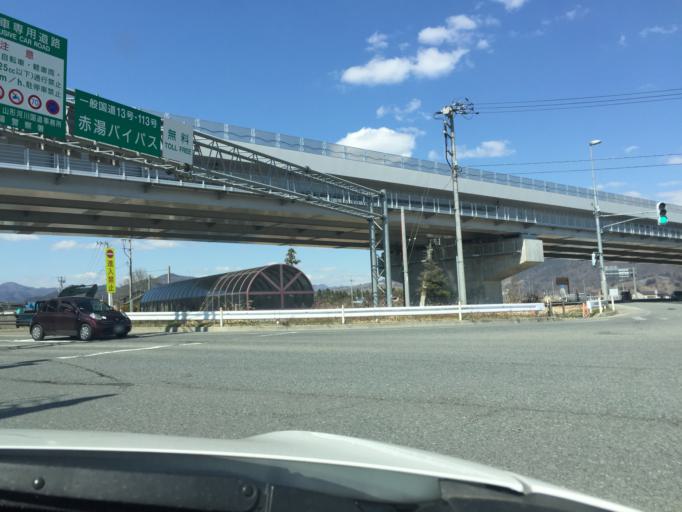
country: JP
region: Yamagata
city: Takahata
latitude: 38.0264
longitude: 140.1685
